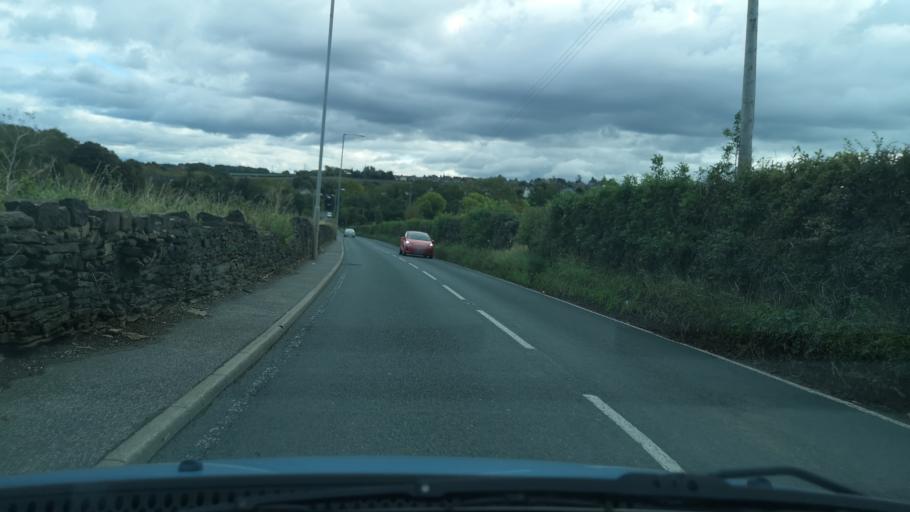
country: GB
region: England
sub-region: City and Borough of Wakefield
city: Middlestown
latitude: 53.6581
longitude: -1.5864
